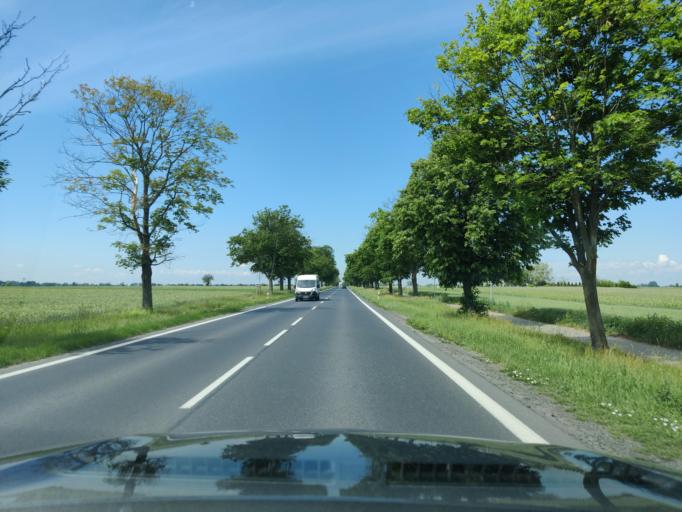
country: PL
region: Greater Poland Voivodeship
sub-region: Powiat grodziski
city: Kamieniec
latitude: 52.2255
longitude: 16.4337
